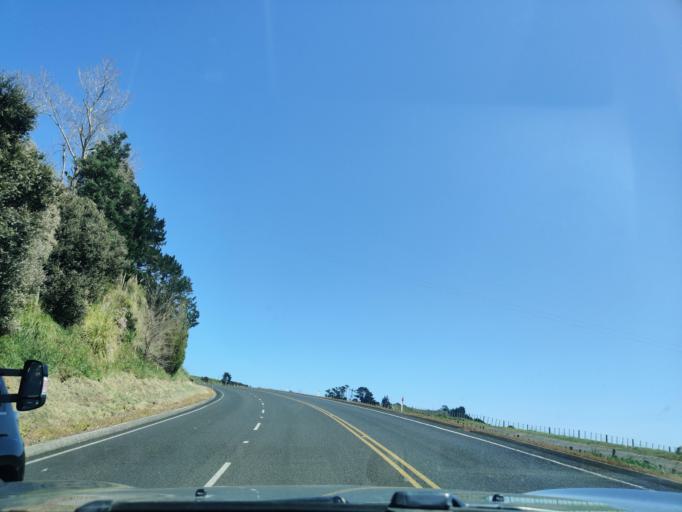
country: NZ
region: Taranaki
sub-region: South Taranaki District
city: Patea
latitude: -39.8036
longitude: 174.7328
